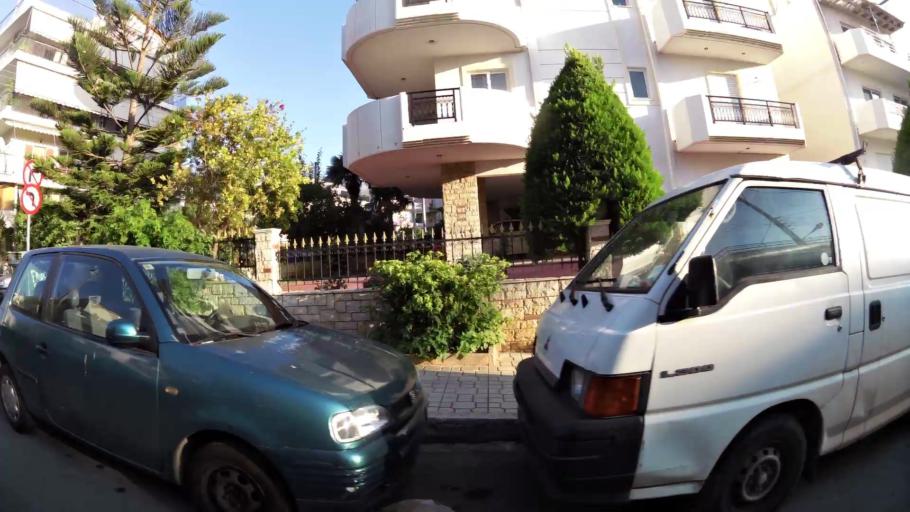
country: GR
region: Attica
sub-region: Nomarchia Athinas
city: Argyroupoli
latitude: 37.9016
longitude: 23.7725
